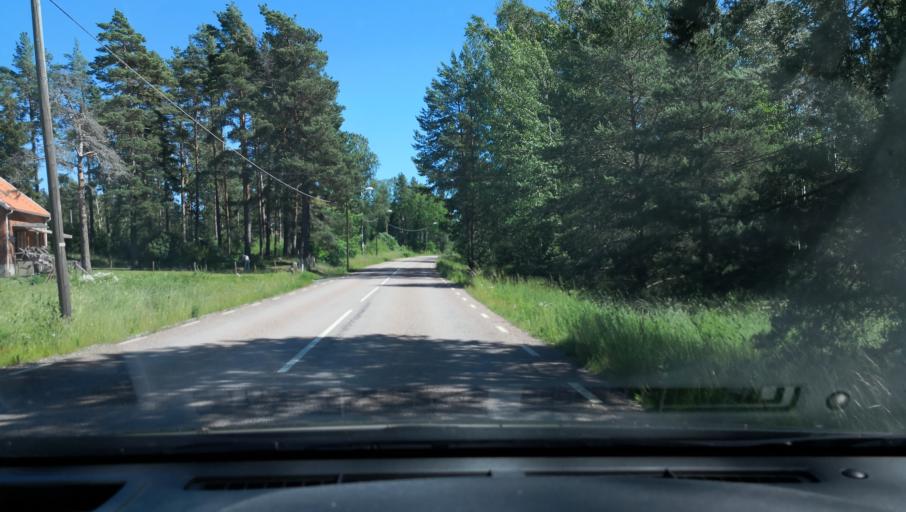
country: SE
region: Vaestmanland
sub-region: Kungsors Kommun
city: Kungsoer
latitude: 59.2917
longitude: 16.0526
